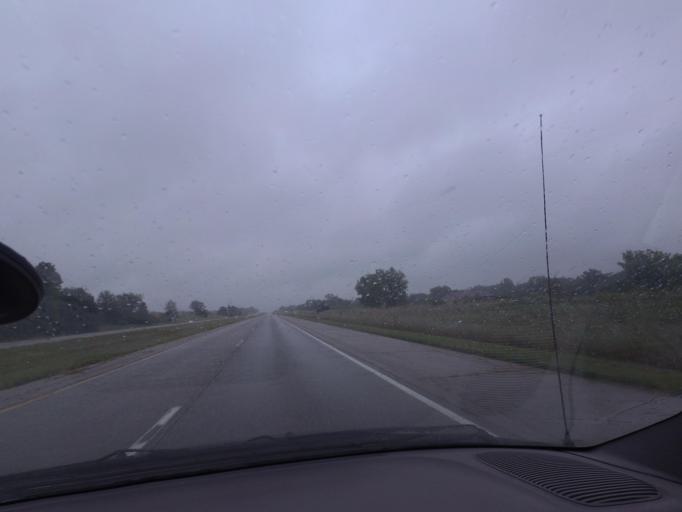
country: US
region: Illinois
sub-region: Pike County
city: Barry
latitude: 39.6891
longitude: -90.9115
